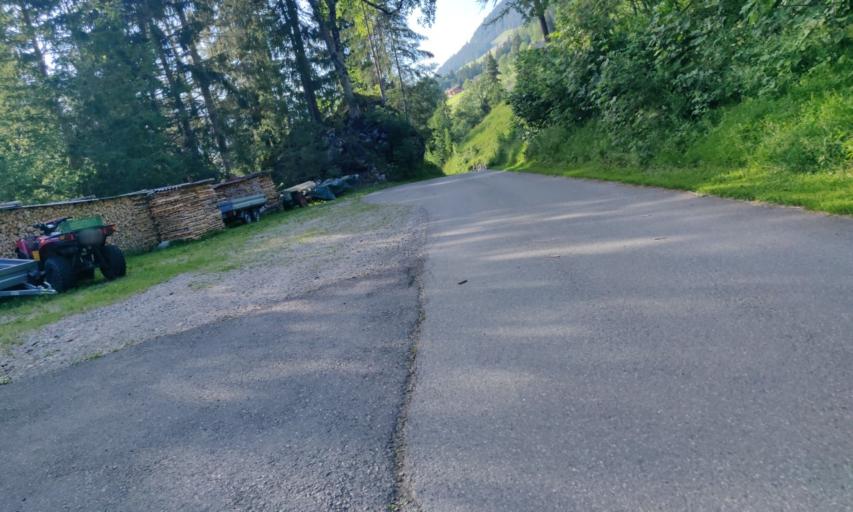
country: CH
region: Bern
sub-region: Obersimmental-Saanen District
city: Gstaad
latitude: 46.4142
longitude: 7.3350
